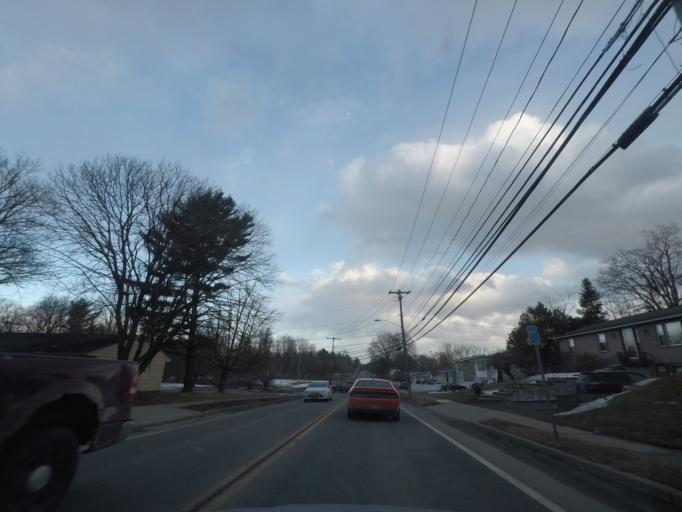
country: US
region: New York
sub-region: Oneida County
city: Utica
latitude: 43.1120
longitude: -75.1915
